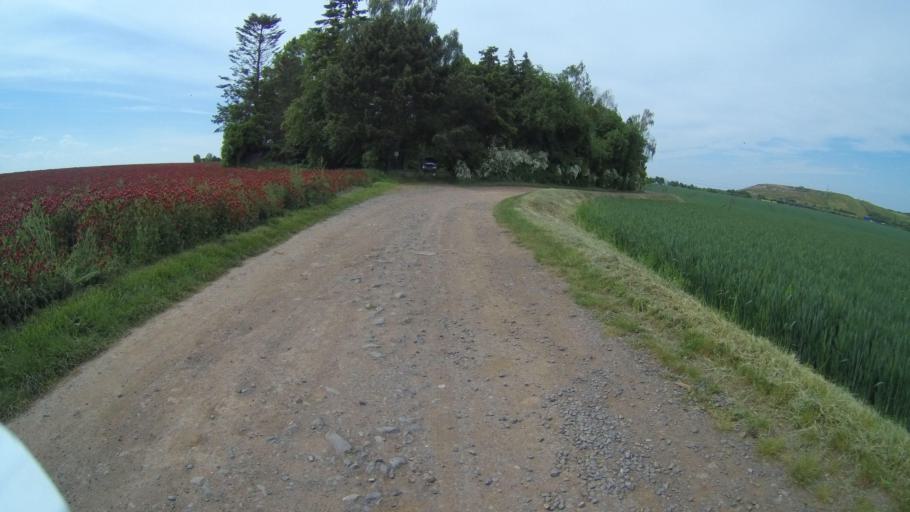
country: CZ
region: Central Bohemia
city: Zdiby
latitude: 50.1487
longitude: 14.4704
